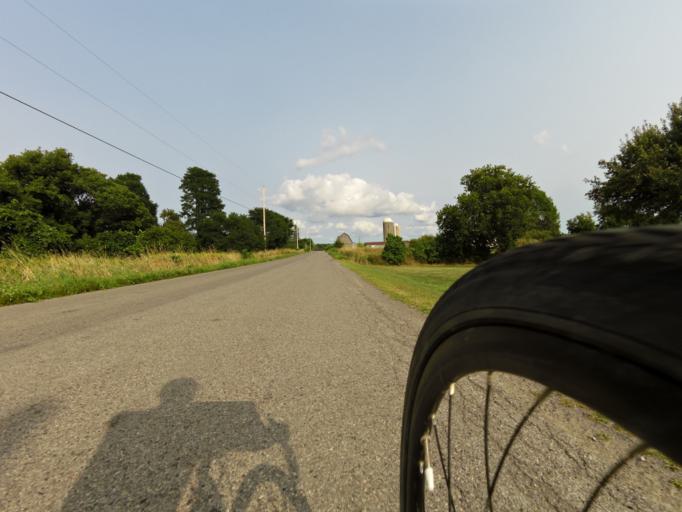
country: CA
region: Ontario
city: Quinte West
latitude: 44.0561
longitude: -77.6488
